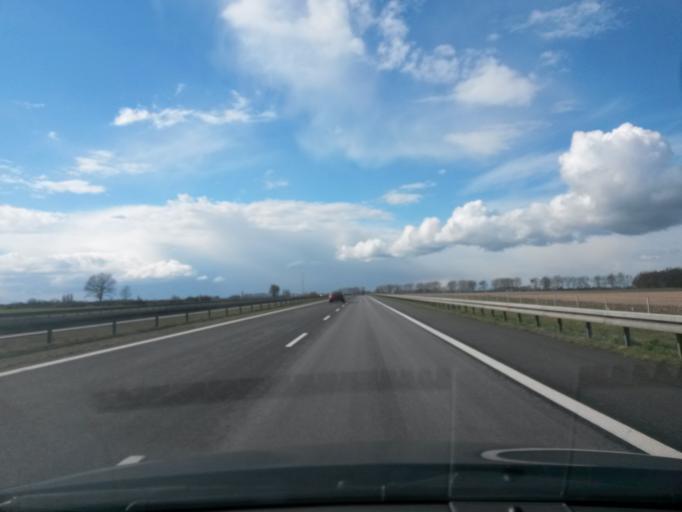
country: PL
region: Greater Poland Voivodeship
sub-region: Powiat wrzesinski
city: Kolaczkowo
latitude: 52.2843
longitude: 17.6842
